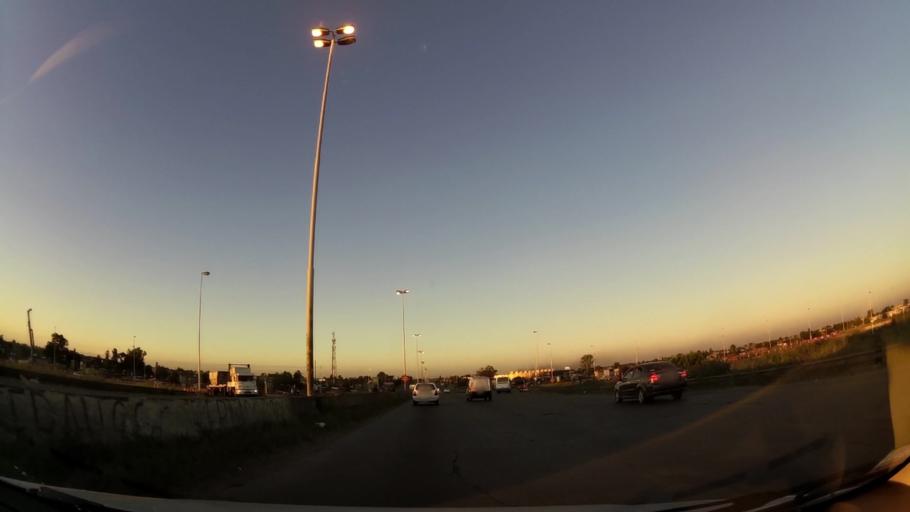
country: AR
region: Buenos Aires
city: Pontevedra
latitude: -34.7595
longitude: -58.6158
